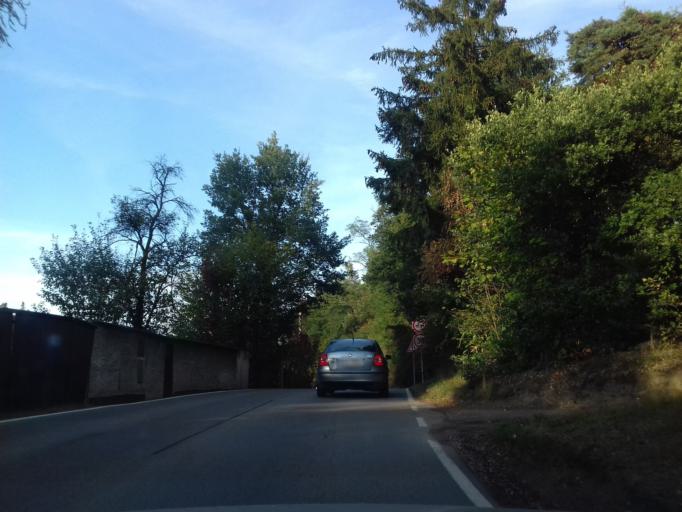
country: CZ
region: Central Bohemia
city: Kamenny Privoz
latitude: 49.8738
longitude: 14.5013
